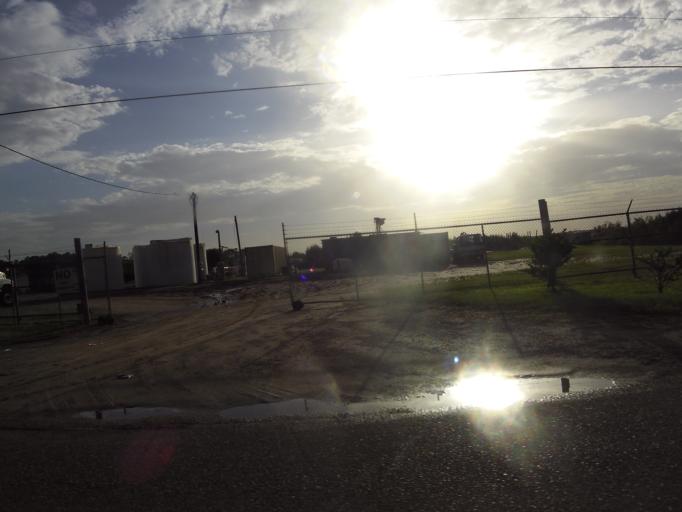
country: US
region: Florida
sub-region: Nassau County
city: Nassau Village-Ratliff
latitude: 30.4032
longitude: -81.7733
